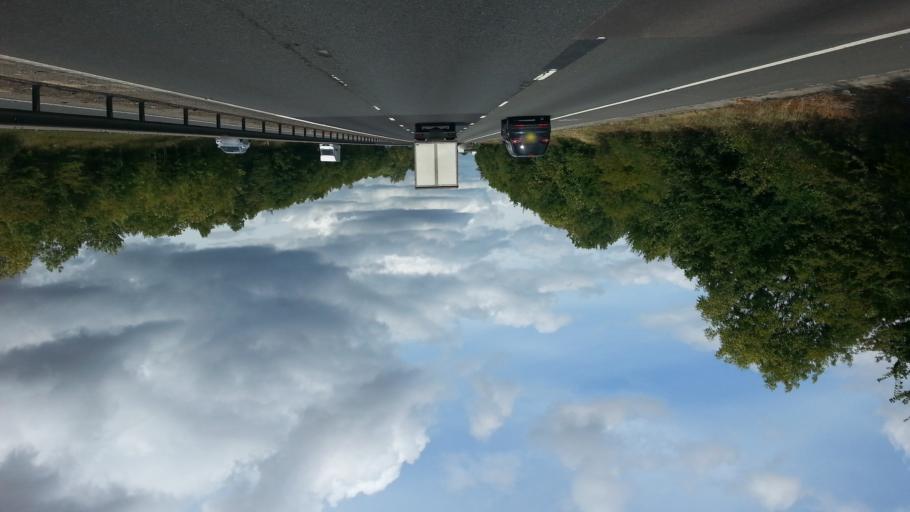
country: GB
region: England
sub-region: Hertfordshire
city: Sawbridgeworth
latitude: 51.7777
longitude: 0.1647
